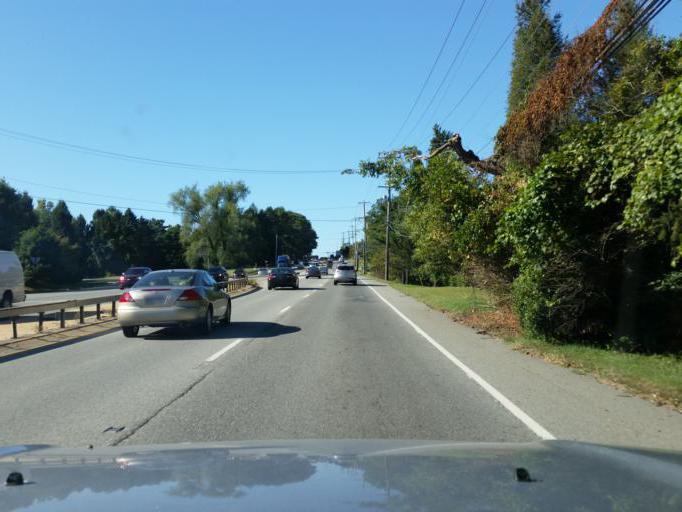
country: US
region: Pennsylvania
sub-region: Chester County
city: West Chester
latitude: 39.9254
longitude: -75.5819
